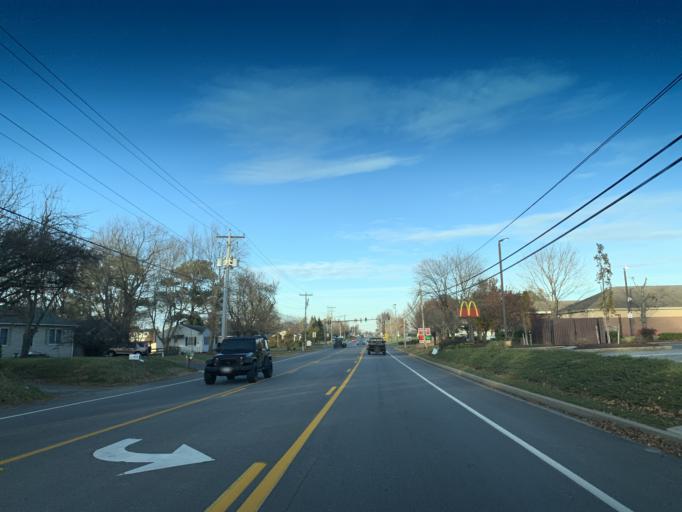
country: US
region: Maryland
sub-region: Kent County
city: Chestertown
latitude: 39.2304
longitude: -76.0723
